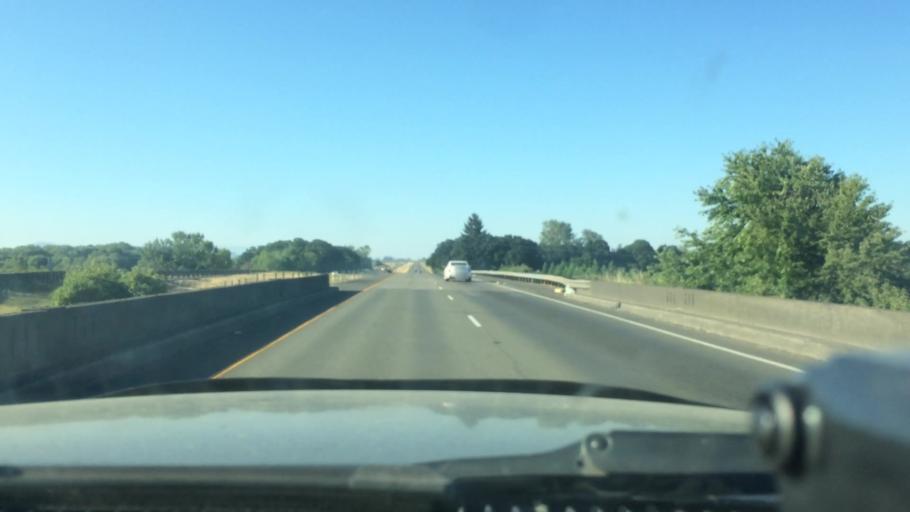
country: US
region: Oregon
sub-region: Linn County
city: Albany
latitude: 44.5959
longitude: -123.0622
